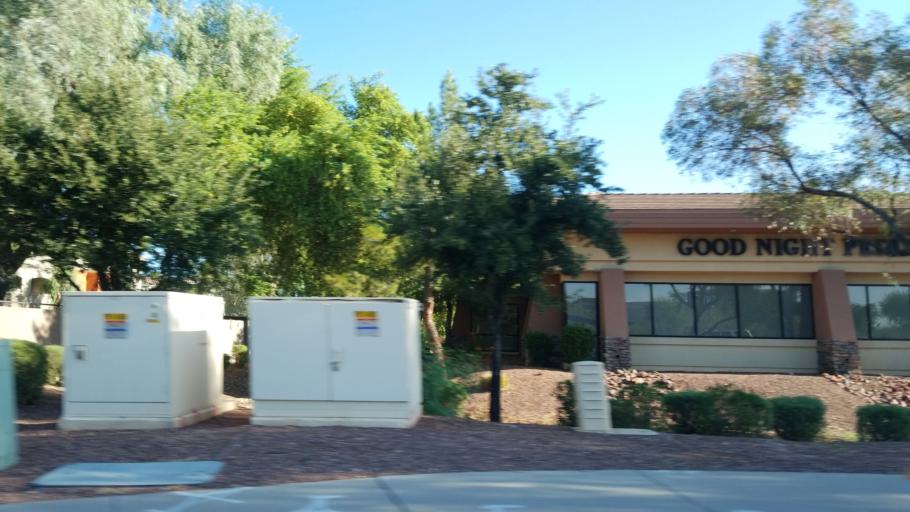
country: US
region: Arizona
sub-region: Maricopa County
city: Tolleson
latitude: 33.4647
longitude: -112.2828
